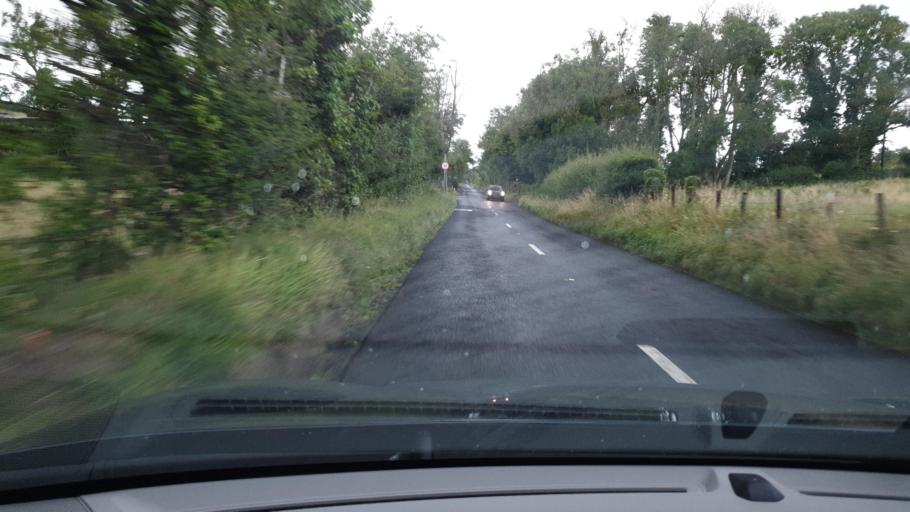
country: IE
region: Leinster
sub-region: South Dublin
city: Rathcoole
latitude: 53.2660
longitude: -6.4919
